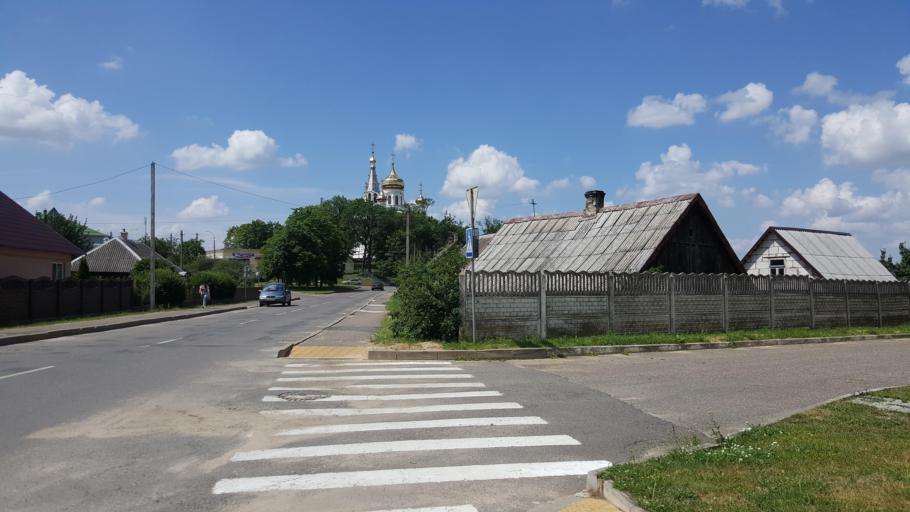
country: BY
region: Brest
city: Kamyanyets
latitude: 52.4036
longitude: 23.8261
